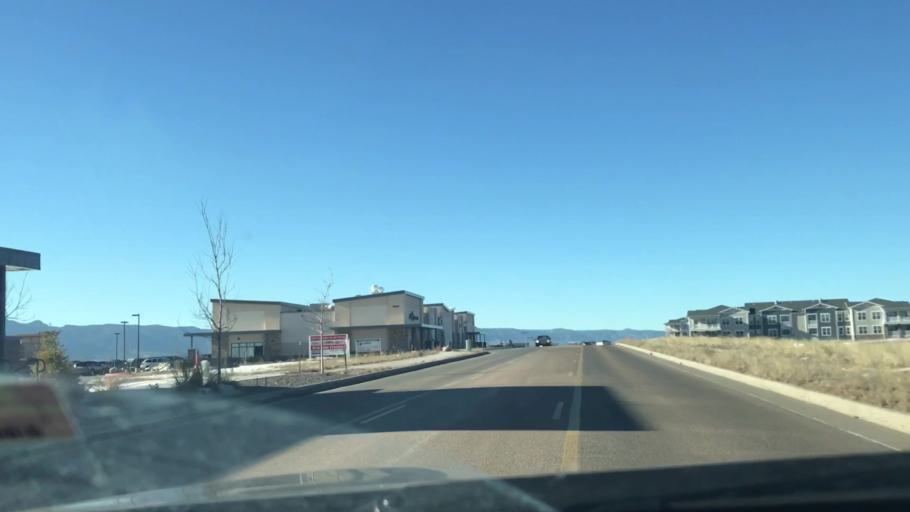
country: US
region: Colorado
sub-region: El Paso County
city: Black Forest
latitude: 38.9716
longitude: -104.7422
